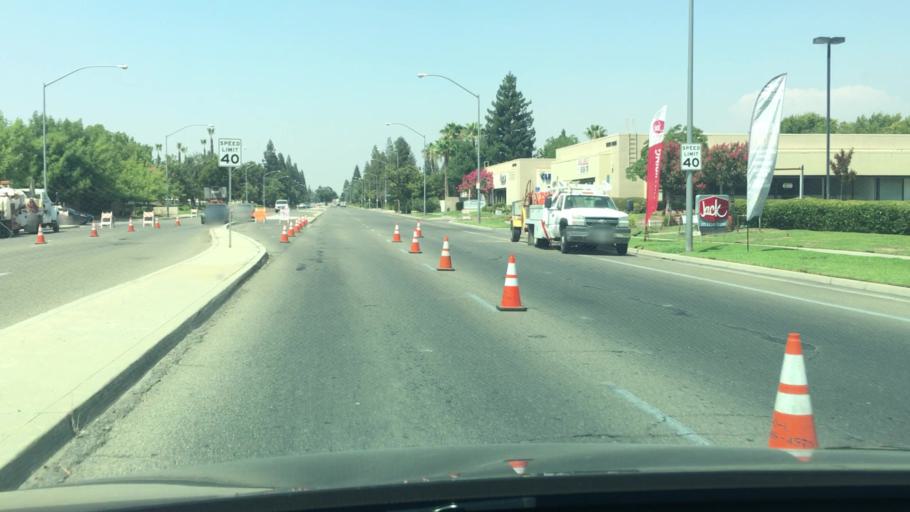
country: US
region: California
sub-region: Fresno County
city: Clovis
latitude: 36.8527
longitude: -119.7567
